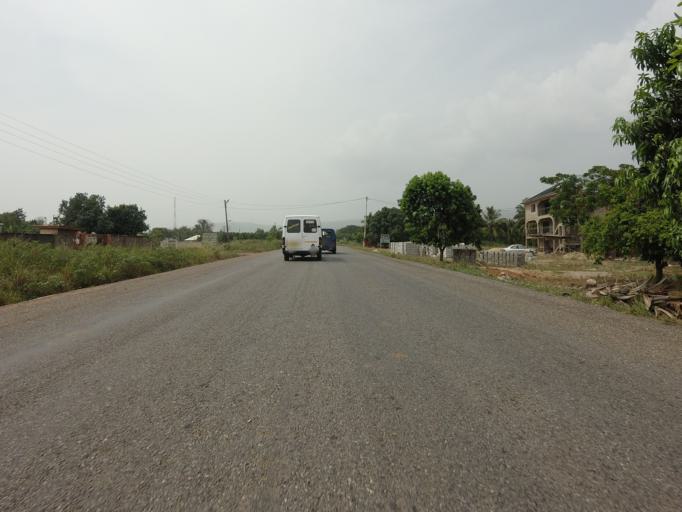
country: GH
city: Akropong
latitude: 6.1029
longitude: -0.0020
